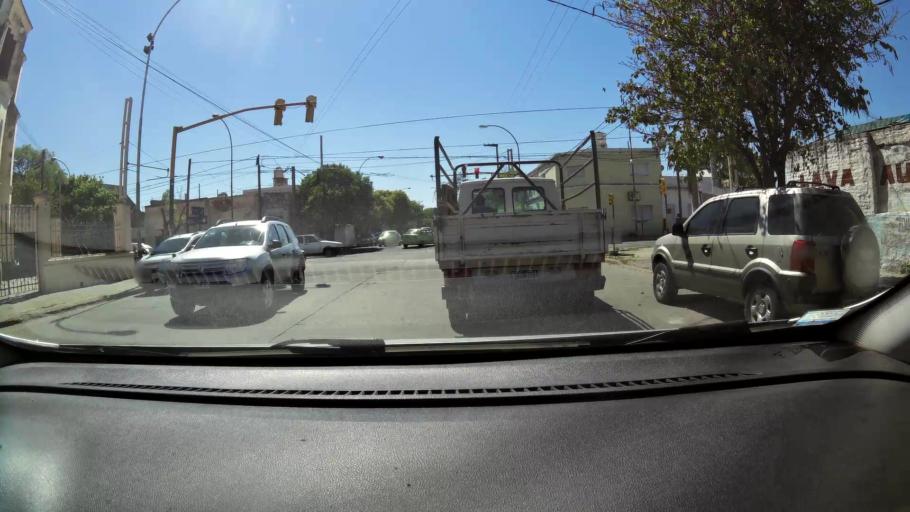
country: AR
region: Cordoba
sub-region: Departamento de Capital
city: Cordoba
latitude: -31.4225
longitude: -64.1570
